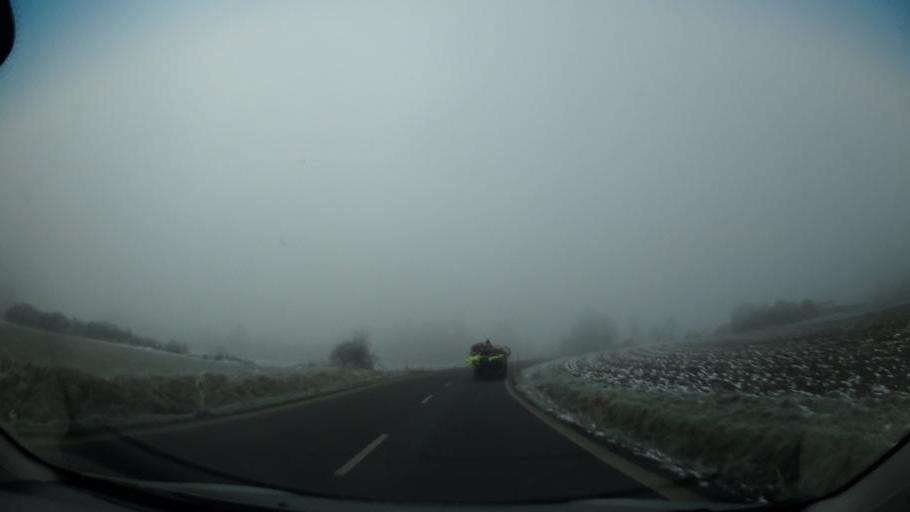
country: CZ
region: Vysocina
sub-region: Okres Trebic
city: Trebic
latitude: 49.2446
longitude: 15.9005
